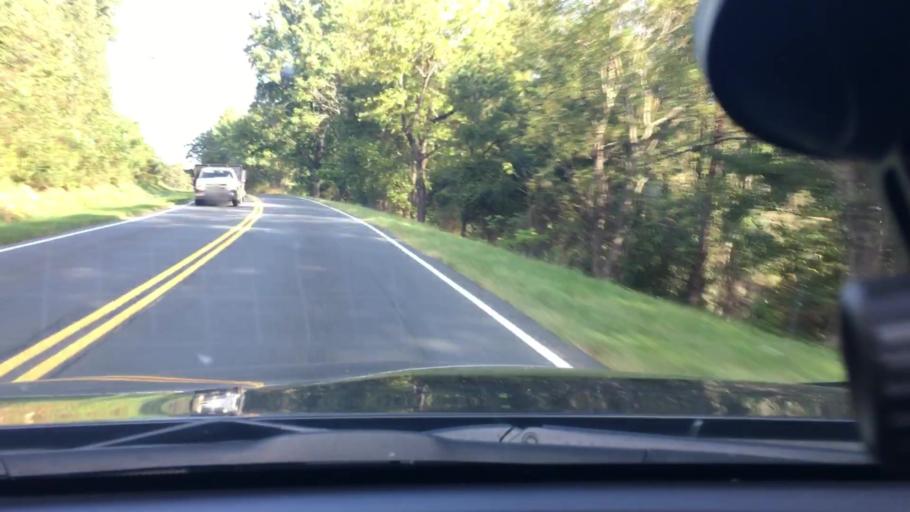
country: US
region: North Carolina
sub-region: Stanly County
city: Albemarle
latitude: 35.3367
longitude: -80.1356
